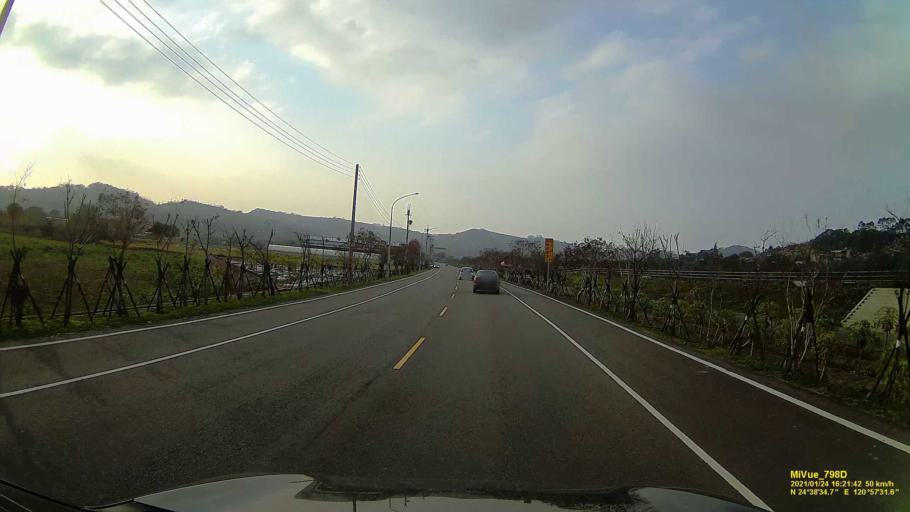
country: TW
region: Taiwan
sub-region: Miaoli
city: Miaoli
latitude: 24.6432
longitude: 120.9584
